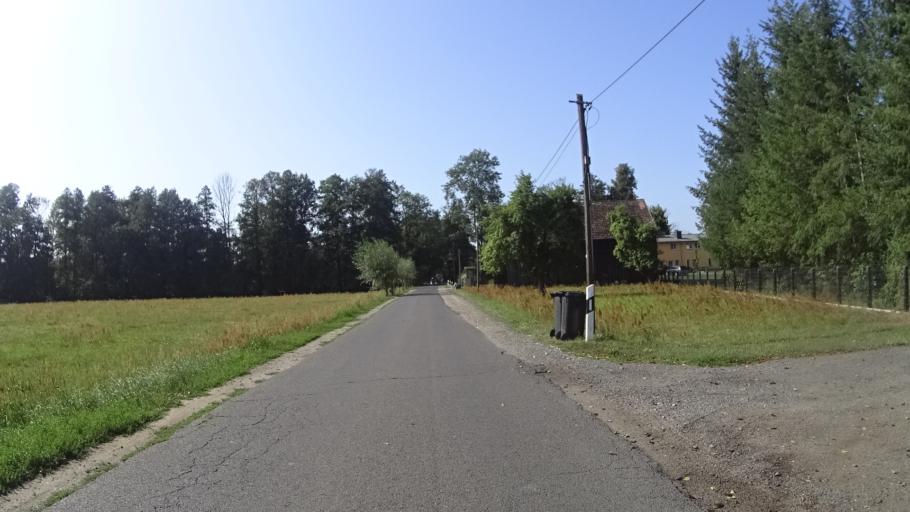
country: DE
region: Brandenburg
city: Straupitz
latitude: 51.8759
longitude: 14.1190
